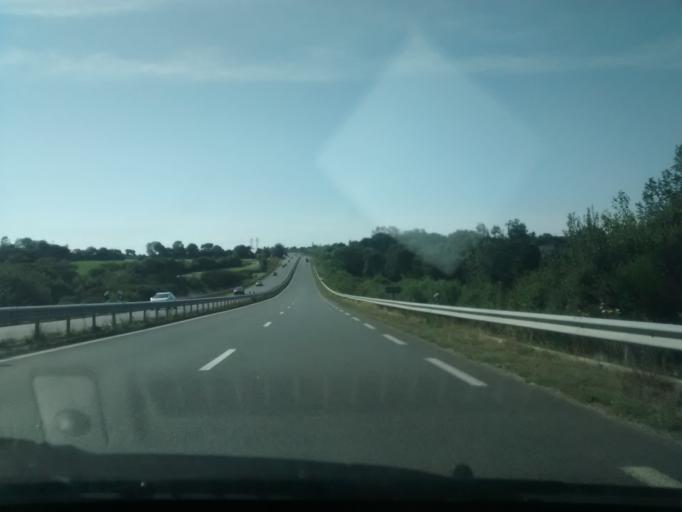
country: FR
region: Brittany
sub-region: Departement des Cotes-d'Armor
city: Rospez
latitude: 48.7115
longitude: -3.3882
